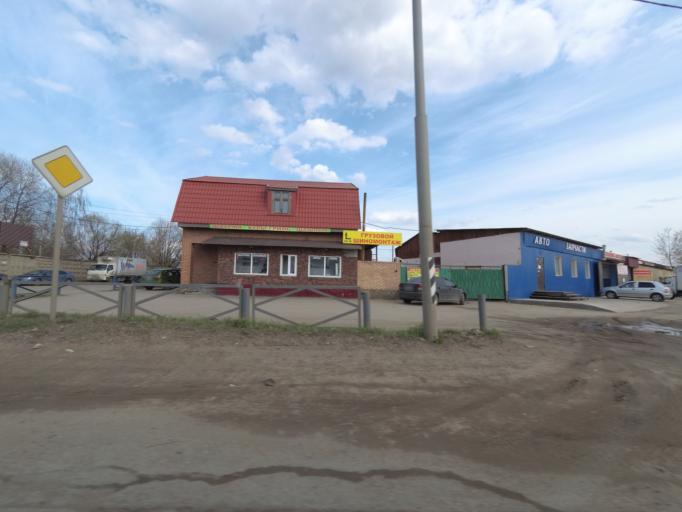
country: RU
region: Moskovskaya
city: Lobnya
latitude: 55.9863
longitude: 37.4172
